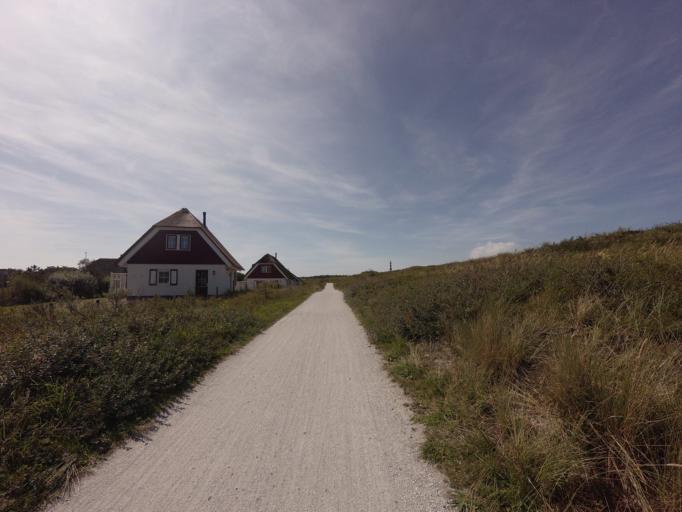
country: NL
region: Friesland
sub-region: Gemeente Ameland
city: Hollum
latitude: 53.4531
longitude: 5.6373
